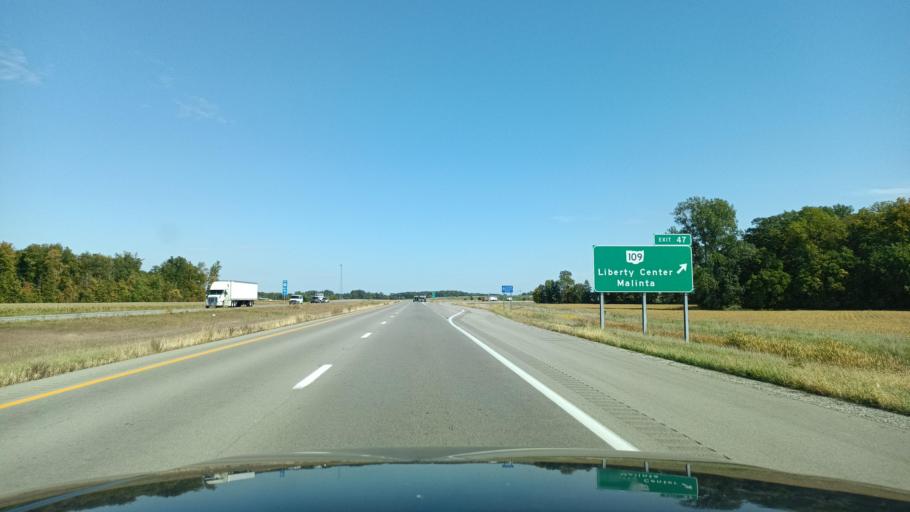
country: US
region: Ohio
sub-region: Henry County
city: Liberty Center
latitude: 41.4261
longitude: -84.0186
